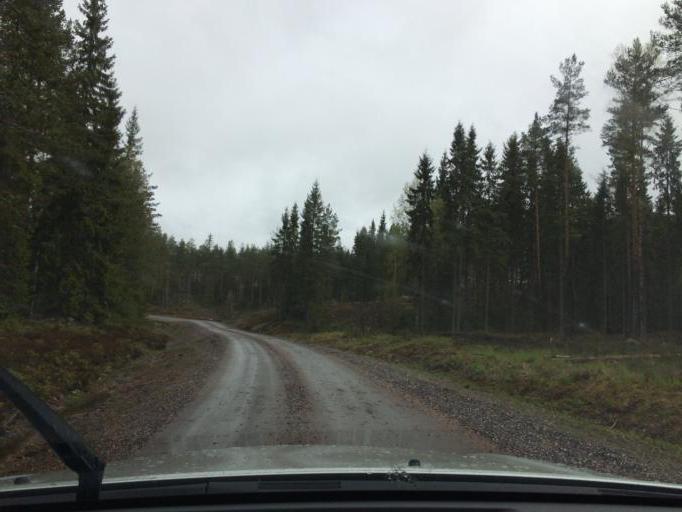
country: SE
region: OErebro
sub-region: Hallefors Kommun
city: Haellefors
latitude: 60.0191
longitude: 14.5690
